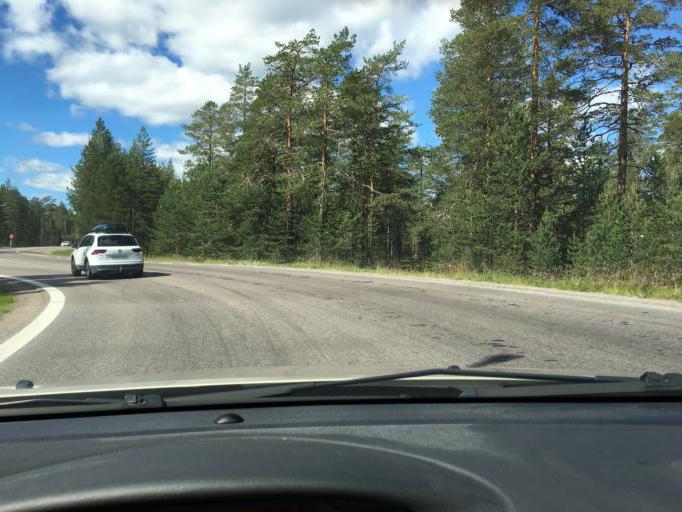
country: SE
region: Norrbotten
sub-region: Lulea Kommun
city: Bergnaset
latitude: 65.5805
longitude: 22.0747
